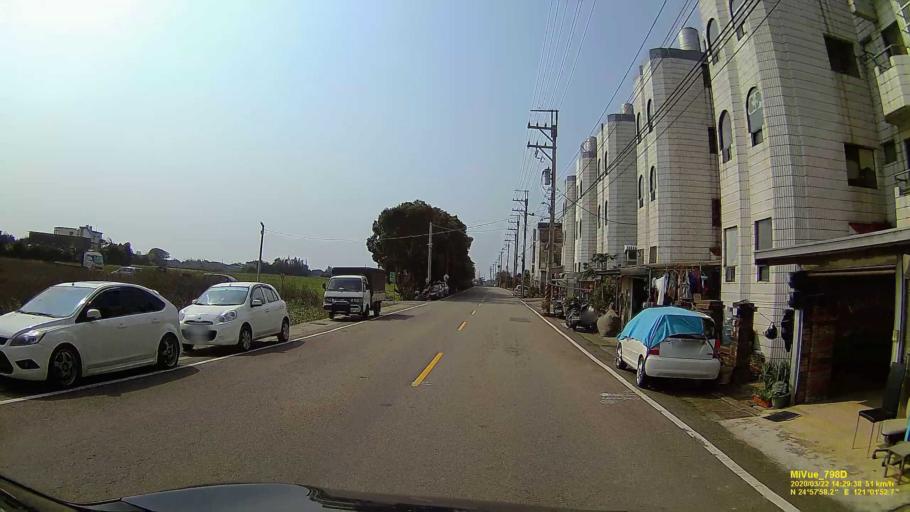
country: TW
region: Taiwan
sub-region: Hsinchu
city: Zhubei
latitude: 24.9663
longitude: 121.0311
